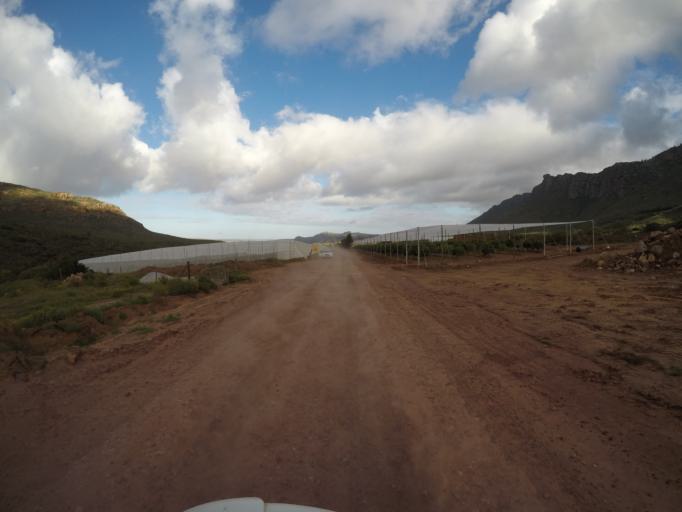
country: ZA
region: Western Cape
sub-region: West Coast District Municipality
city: Clanwilliam
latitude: -32.3408
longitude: 18.7752
